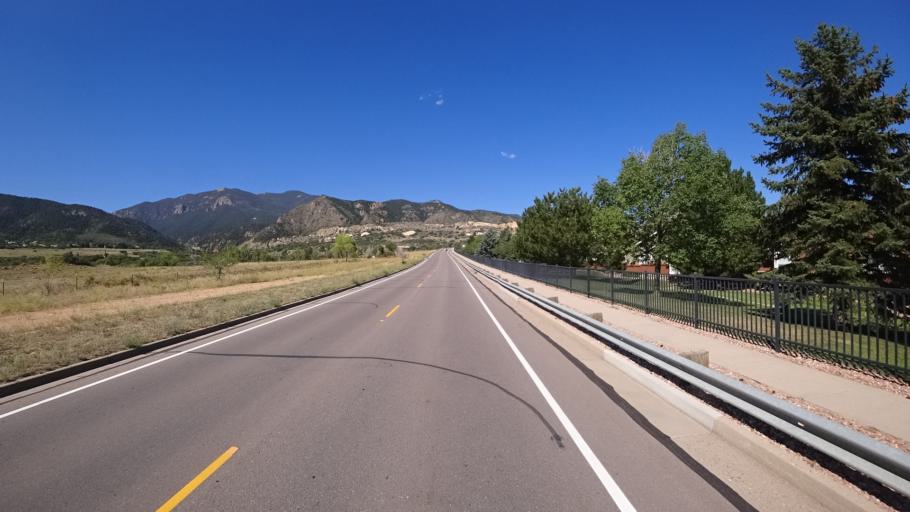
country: US
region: Colorado
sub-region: El Paso County
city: Colorado Springs
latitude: 38.8305
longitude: -104.8731
